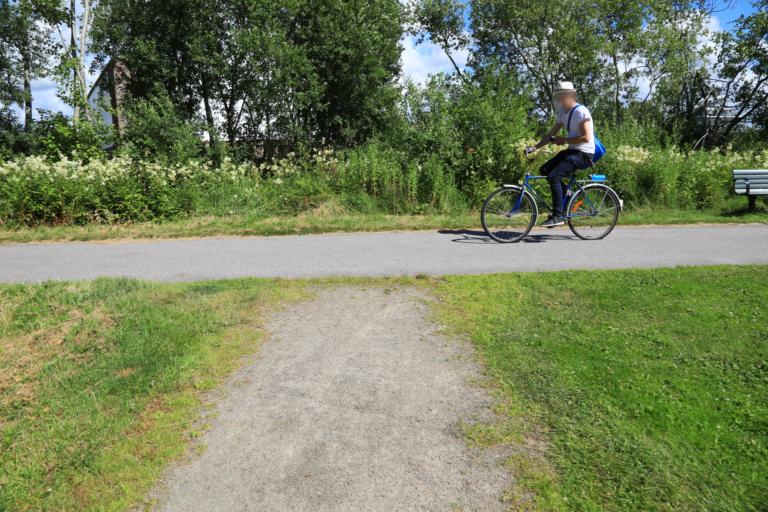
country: SE
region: Halland
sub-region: Varbergs Kommun
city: Traslovslage
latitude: 57.0894
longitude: 12.2754
